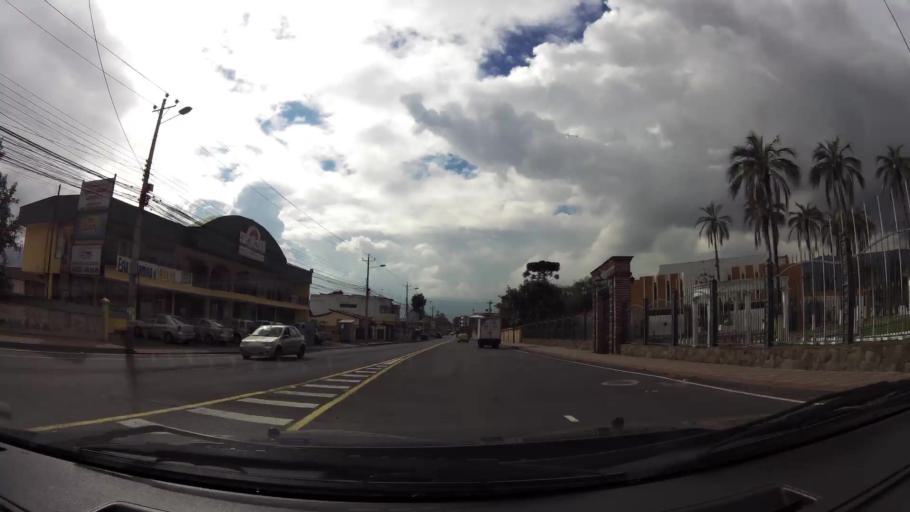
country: EC
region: Pichincha
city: Sangolqui
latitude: -0.3126
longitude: -78.4511
